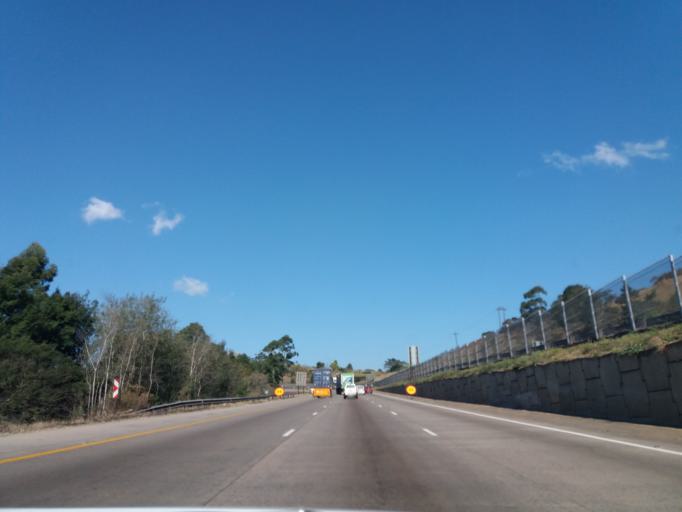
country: ZA
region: KwaZulu-Natal
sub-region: eThekwini Metropolitan Municipality
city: Mpumalanga
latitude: -29.7747
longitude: 30.6957
